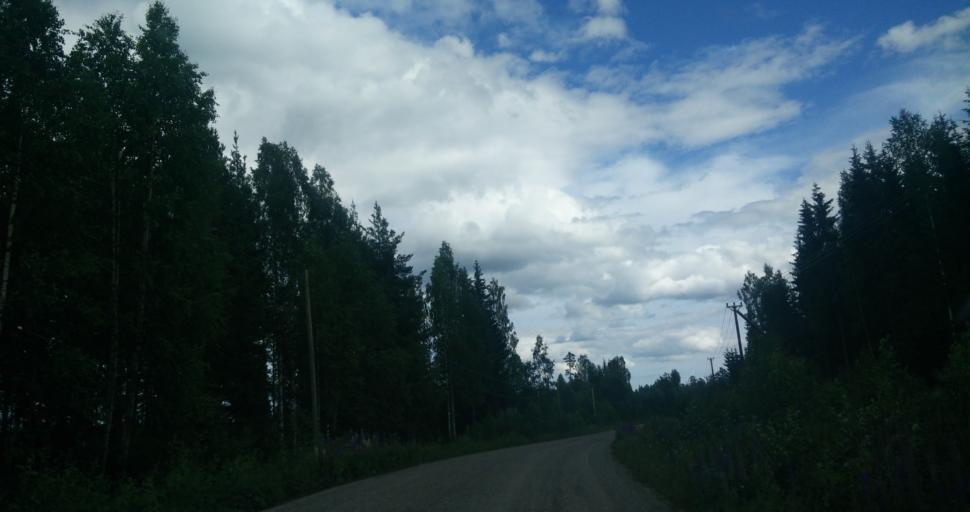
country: SE
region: Gaevleborg
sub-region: Nordanstigs Kommun
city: Bergsjoe
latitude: 62.0584
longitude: 16.8037
